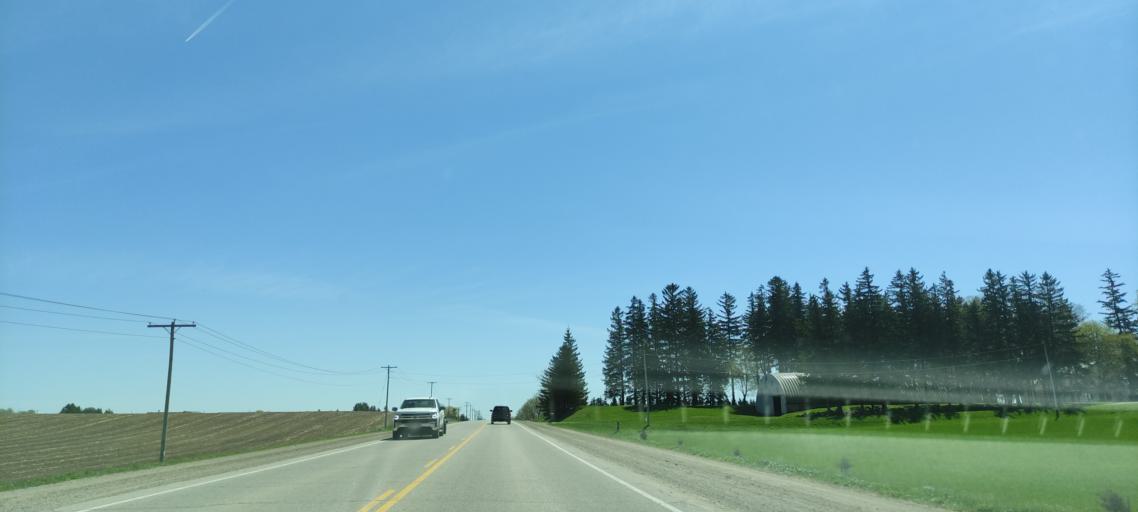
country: CA
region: Ontario
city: Waterloo
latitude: 43.6033
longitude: -80.5947
